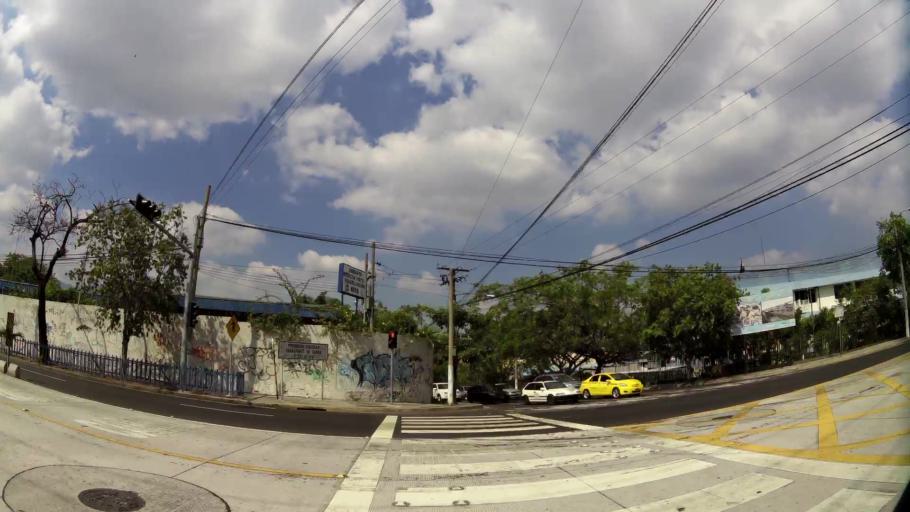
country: SV
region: San Salvador
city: San Salvador
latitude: 13.7034
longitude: -89.2012
